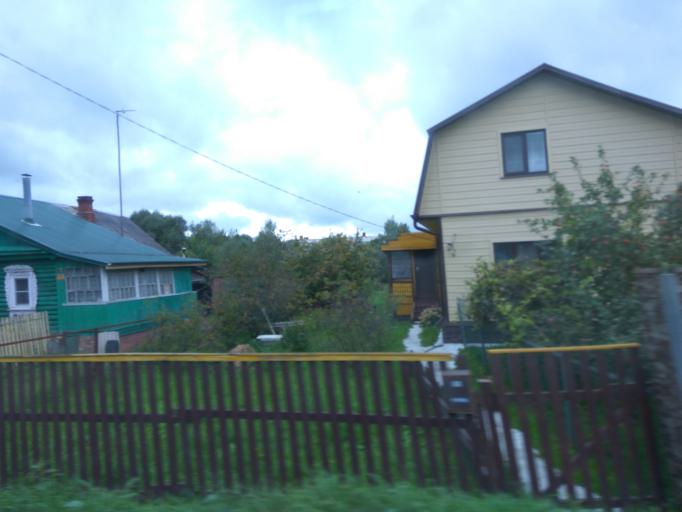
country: RU
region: Moskovskaya
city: Malyshevo
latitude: 55.5063
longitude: 38.3439
